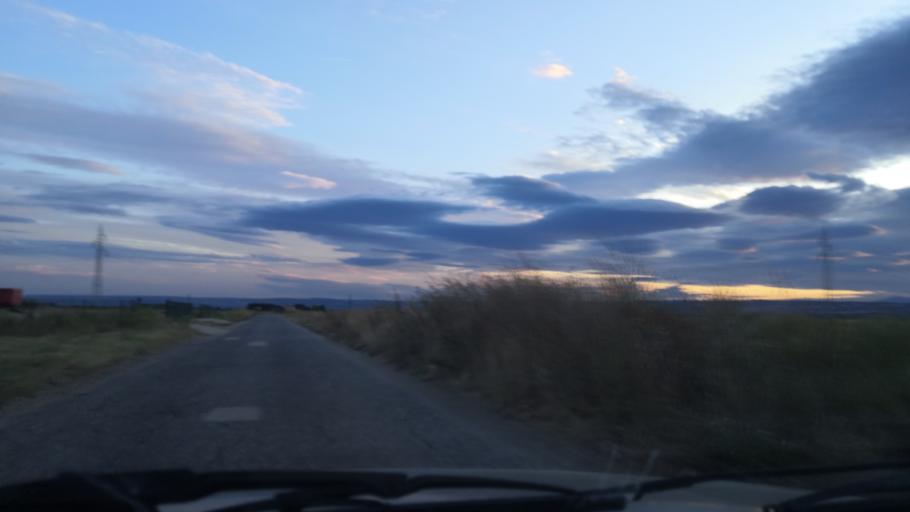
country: RO
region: Mehedinti
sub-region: Comuna Gogosu
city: Balta Verde
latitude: 44.2889
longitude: 22.5802
